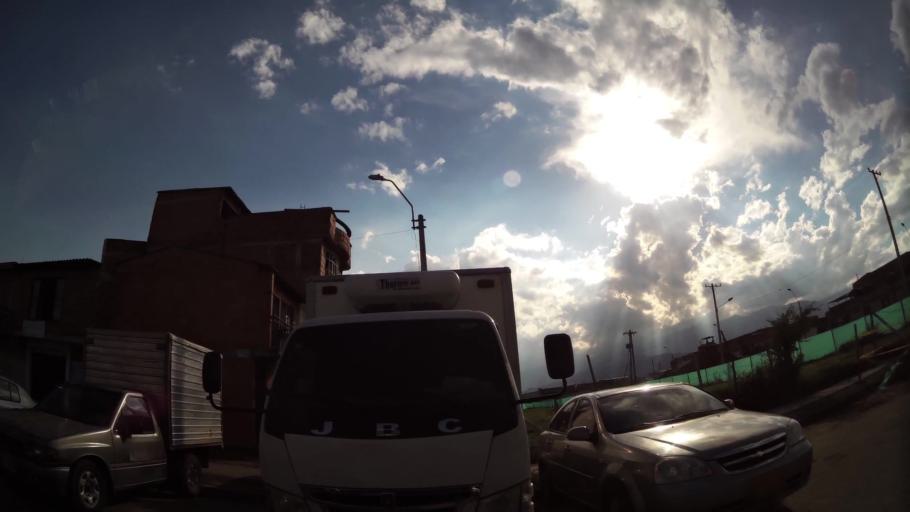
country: CO
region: Valle del Cauca
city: Cali
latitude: 3.3946
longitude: -76.5117
